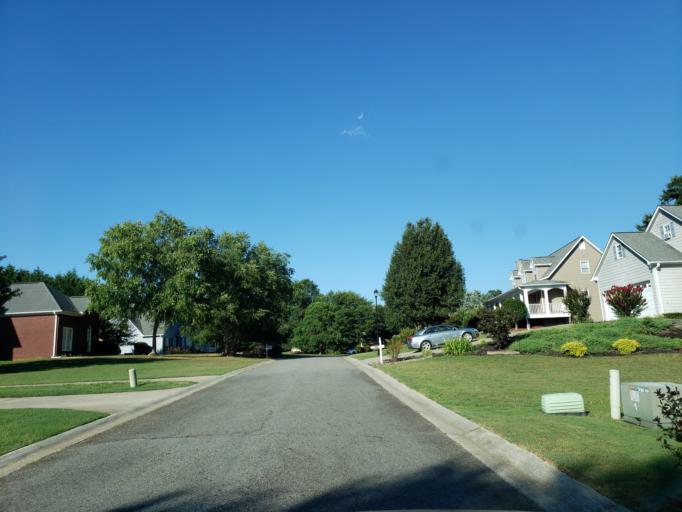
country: US
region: Georgia
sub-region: Bartow County
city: Euharlee
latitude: 34.1066
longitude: -84.9976
